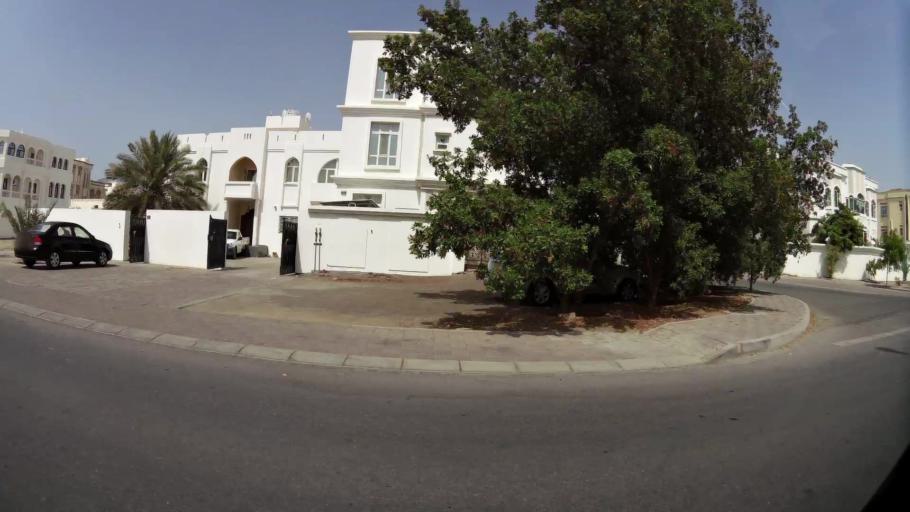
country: OM
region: Muhafazat Masqat
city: Bawshar
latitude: 23.5782
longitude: 58.4027
